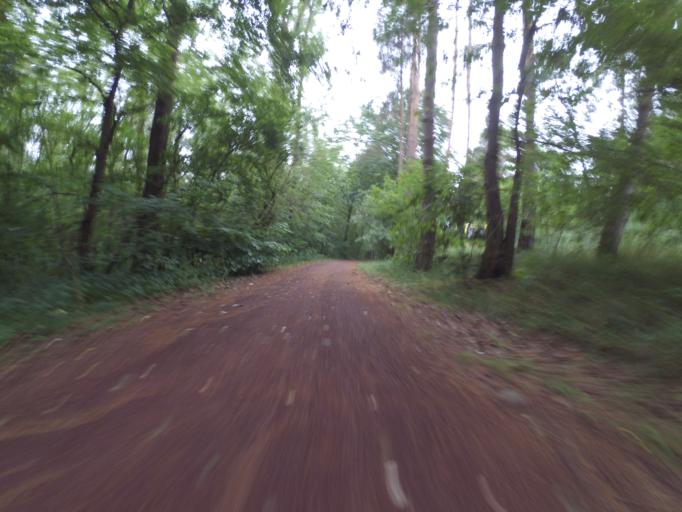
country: DE
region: Mecklenburg-Vorpommern
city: Plau am See
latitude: 53.4766
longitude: 12.2820
